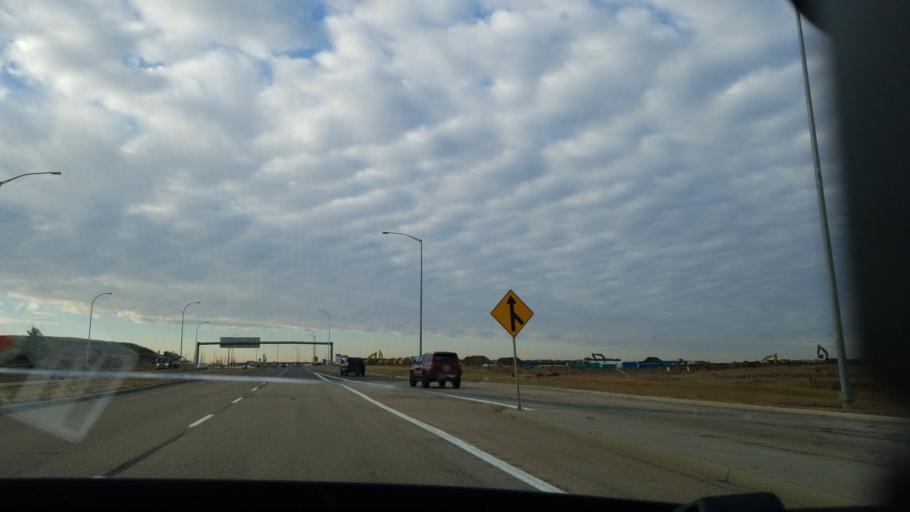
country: CA
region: Alberta
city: Edmonton
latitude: 53.6439
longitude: -113.4408
